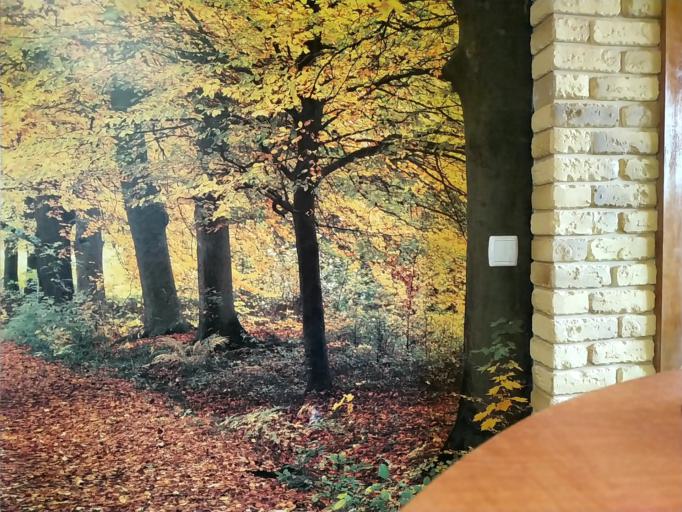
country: RU
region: Novgorod
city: Opechenskiy Posad
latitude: 58.2710
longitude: 34.0068
